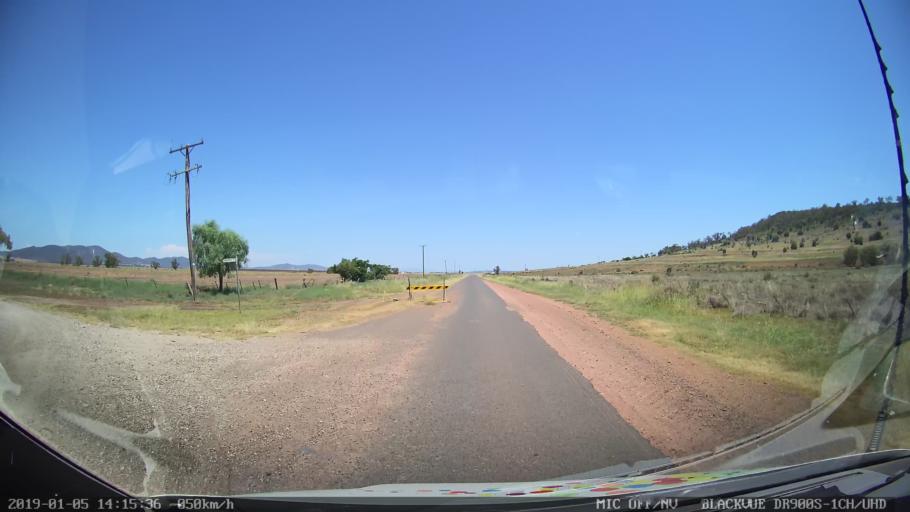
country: AU
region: New South Wales
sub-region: Liverpool Plains
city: Quirindi
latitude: -31.2489
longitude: 150.4714
